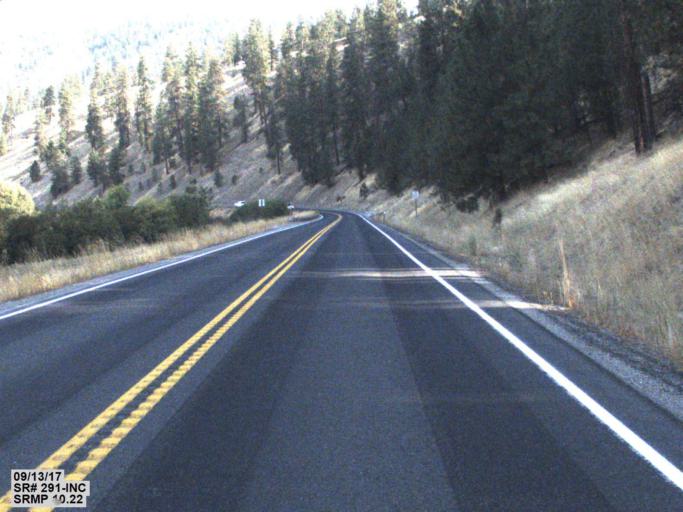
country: US
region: Washington
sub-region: Spokane County
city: Fairwood
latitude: 47.7851
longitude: -117.5284
